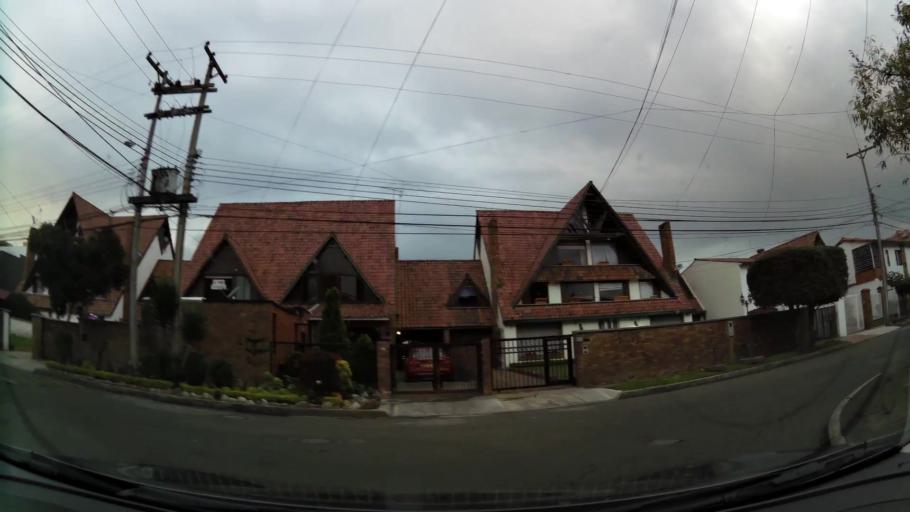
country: CO
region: Bogota D.C.
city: Barrio San Luis
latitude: 4.7257
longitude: -74.0648
